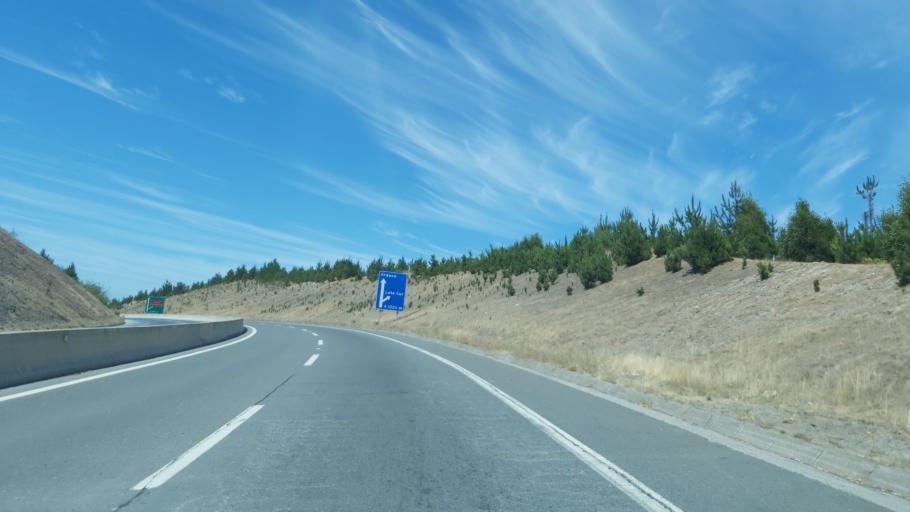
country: CL
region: Biobio
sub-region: Provincia de Concepcion
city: Lota
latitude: -37.0920
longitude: -73.1395
